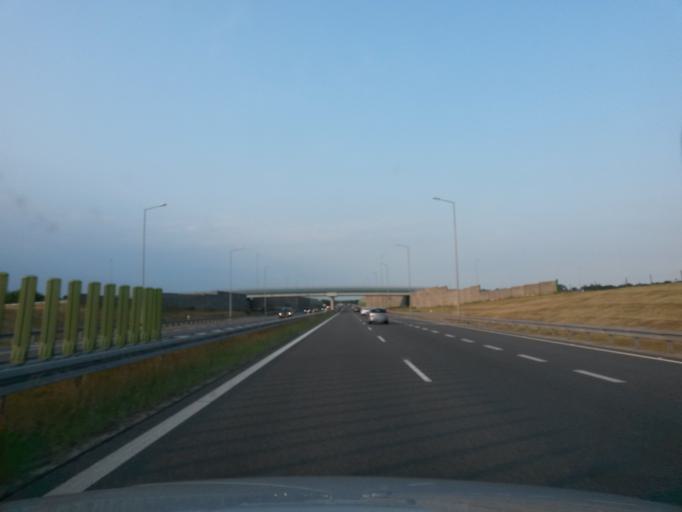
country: PL
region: Lower Silesian Voivodeship
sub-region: Powiat olesnicki
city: Olesnica
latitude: 51.2415
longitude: 17.5027
